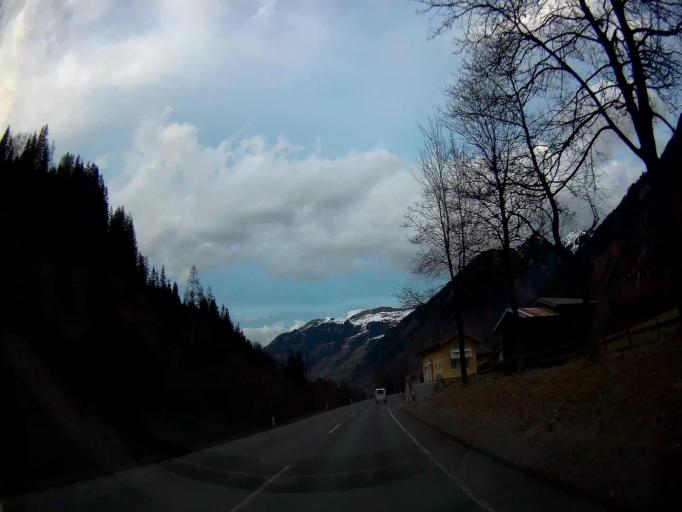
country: AT
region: Salzburg
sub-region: Politischer Bezirk Sankt Johann im Pongau
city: Bad Hofgastein
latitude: 47.2034
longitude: 13.1062
